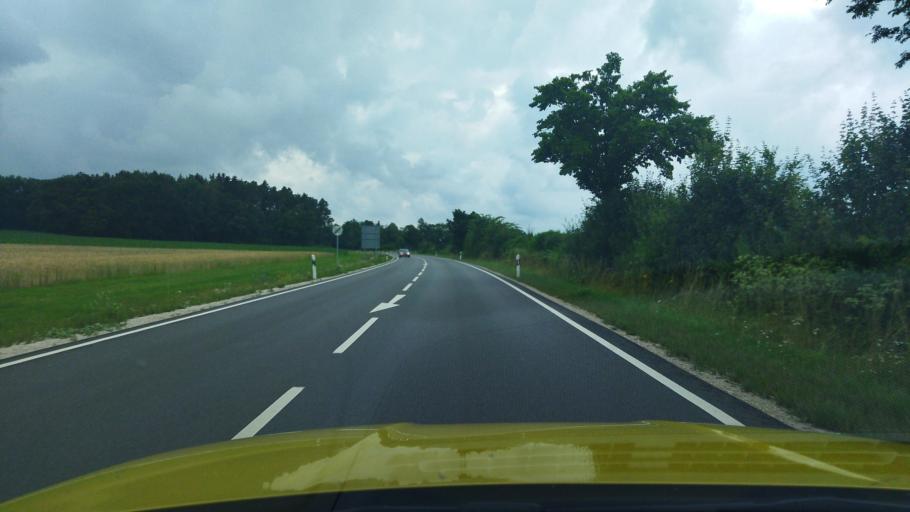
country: DE
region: Bavaria
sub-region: Regierungsbezirk Mittelfranken
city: Absberg
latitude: 49.1100
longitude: 10.9105
